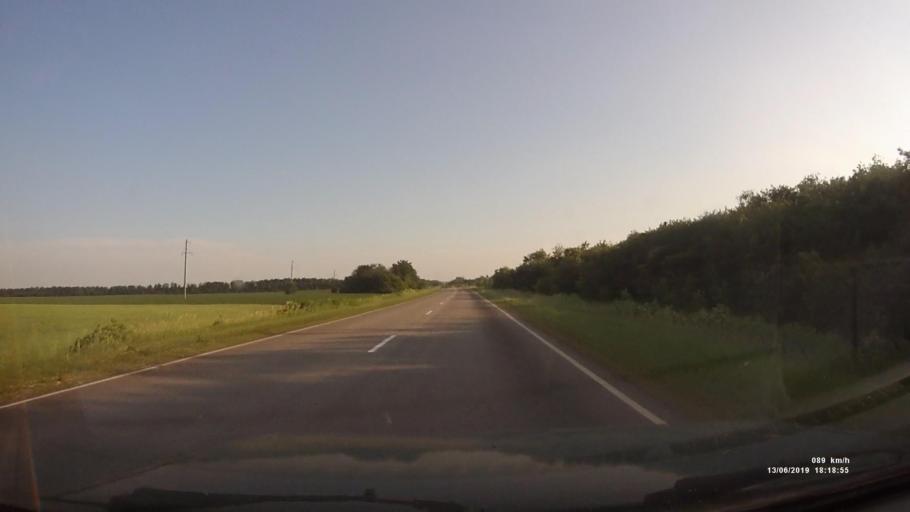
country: RU
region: Rostov
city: Kazanskaya
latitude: 49.9025
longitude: 41.3097
